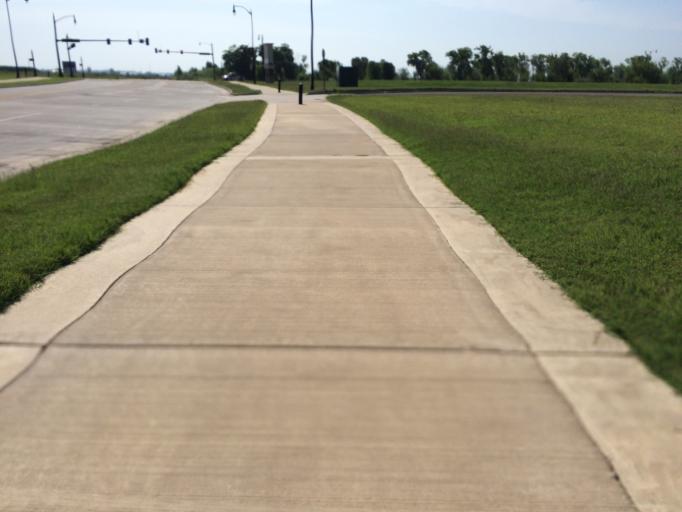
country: US
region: Oklahoma
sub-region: Cleveland County
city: Norman
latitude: 35.2475
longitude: -97.4807
